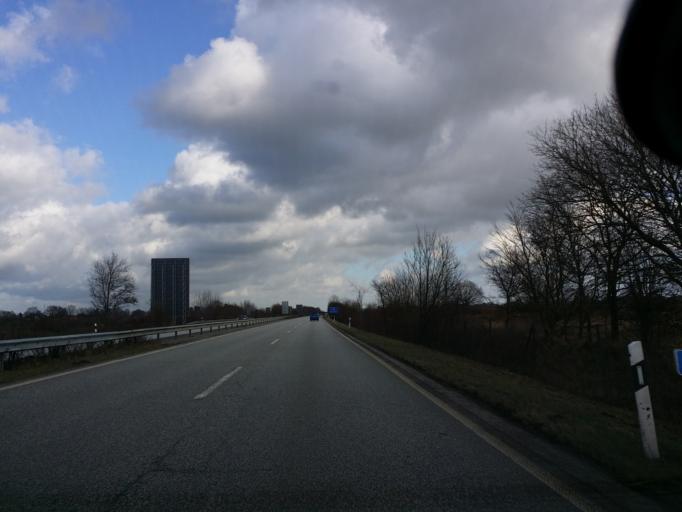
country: DE
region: Schleswig-Holstein
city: Schulldorf
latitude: 54.3089
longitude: 9.7699
